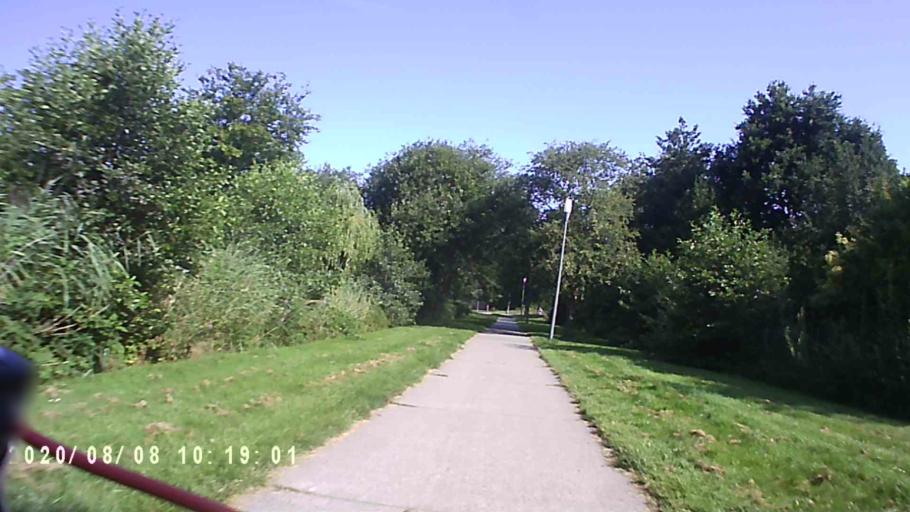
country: NL
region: Groningen
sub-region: Gemeente Leek
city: Leek
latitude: 53.1353
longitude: 6.4010
